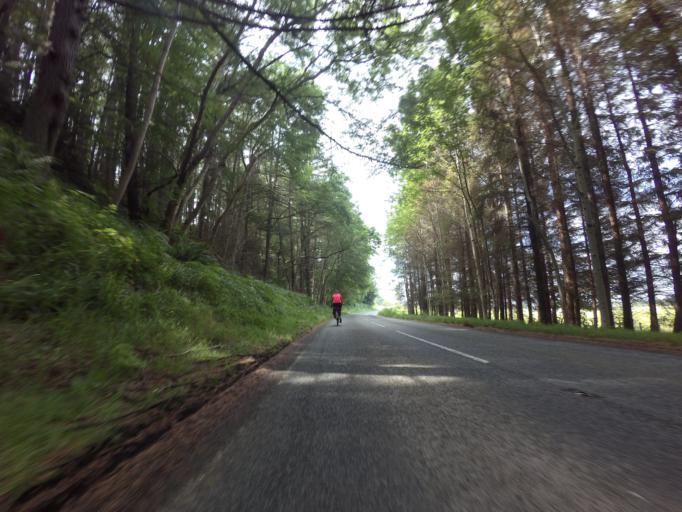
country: GB
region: Scotland
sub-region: Highland
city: Tain
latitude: 57.8268
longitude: -4.1409
